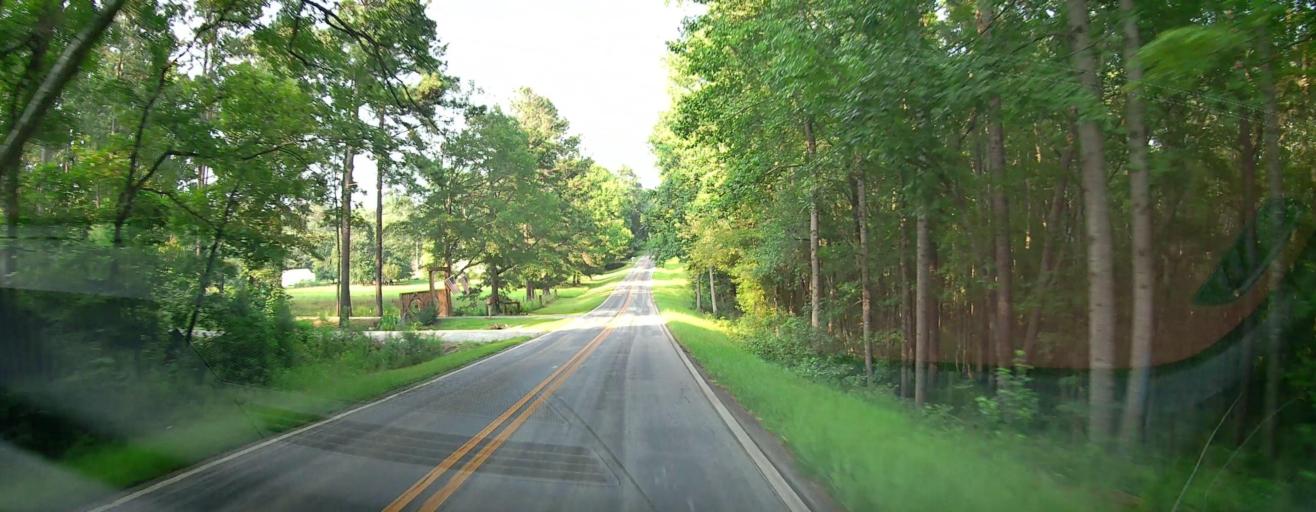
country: US
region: Georgia
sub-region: Jones County
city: Gray
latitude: 33.0992
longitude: -83.6769
